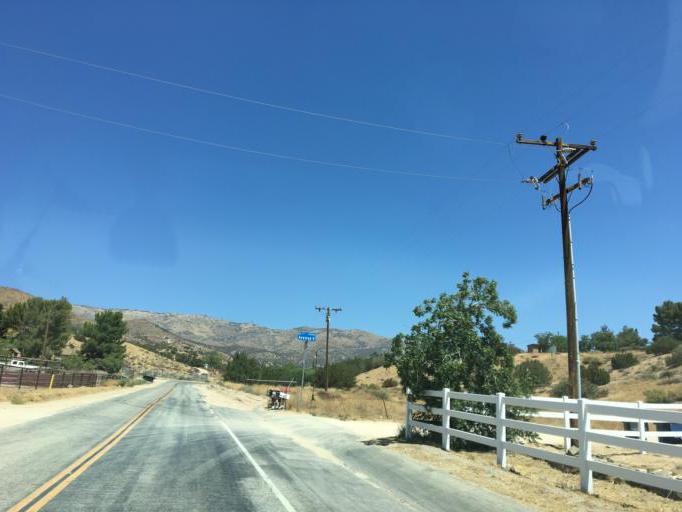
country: US
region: California
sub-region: Los Angeles County
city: Acton
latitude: 34.5096
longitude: -118.2160
